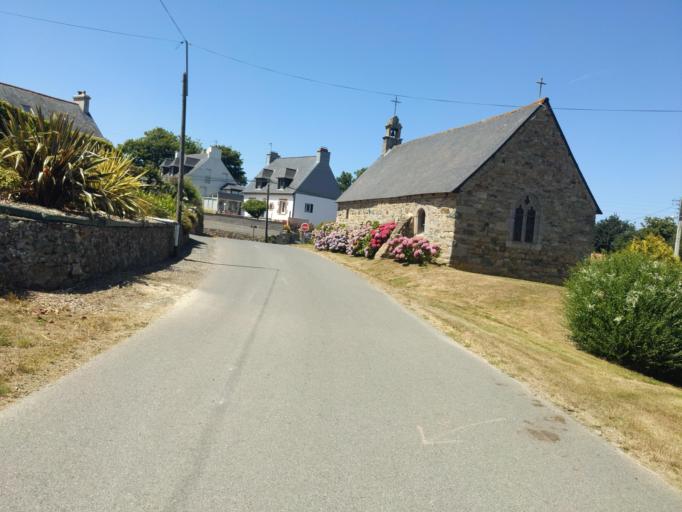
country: FR
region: Brittany
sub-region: Departement des Cotes-d'Armor
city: Plougrescant
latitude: 48.8234
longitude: -3.2094
